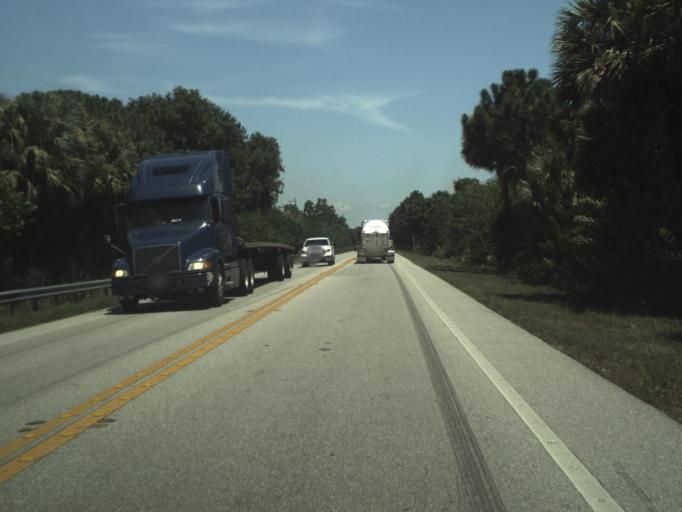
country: US
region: Florida
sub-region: Martin County
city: Indiantown
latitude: 27.1031
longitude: -80.5930
